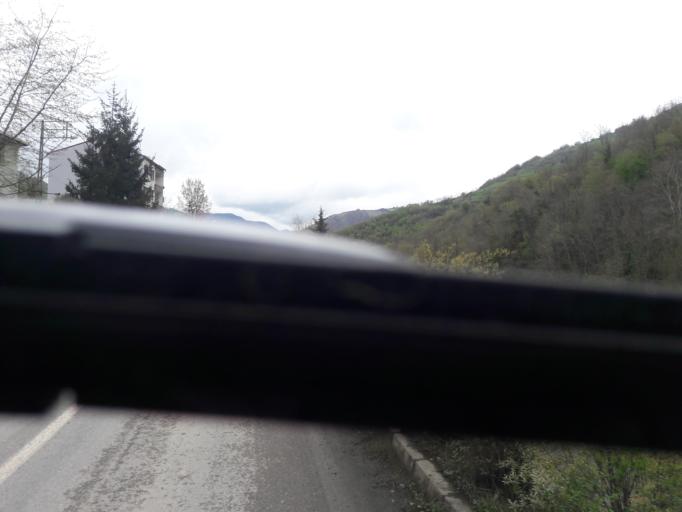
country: TR
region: Trabzon
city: Duzkoy
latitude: 40.9280
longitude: 39.4938
